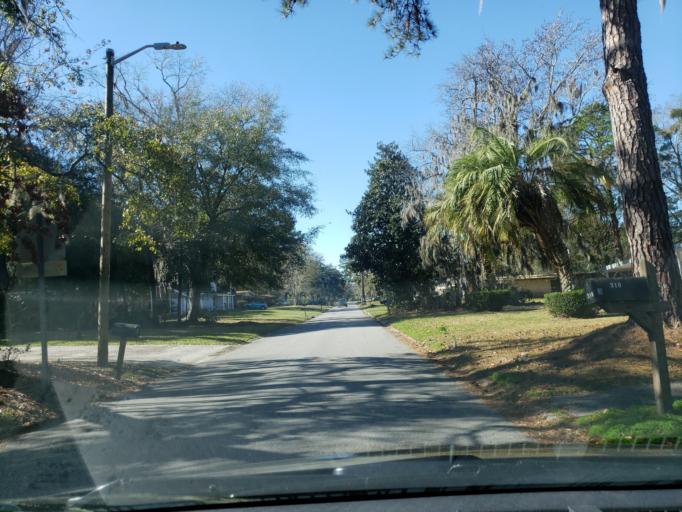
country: US
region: Georgia
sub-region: Chatham County
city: Montgomery
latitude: 31.9709
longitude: -81.1408
